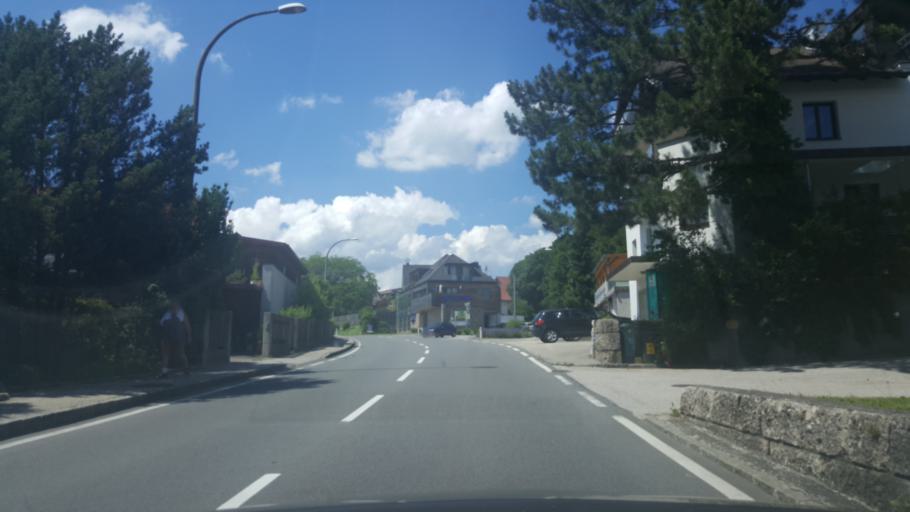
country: AT
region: Upper Austria
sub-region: Politischer Bezirk Vocklabruck
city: Seewalchen
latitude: 47.9507
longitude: 13.5919
